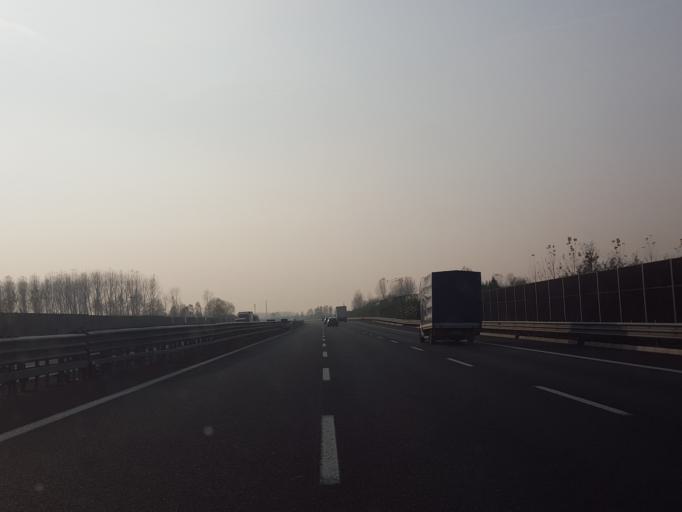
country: IT
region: Veneto
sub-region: Provincia di Venezia
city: Peseggia-Gardigiano
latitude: 45.5768
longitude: 12.1693
